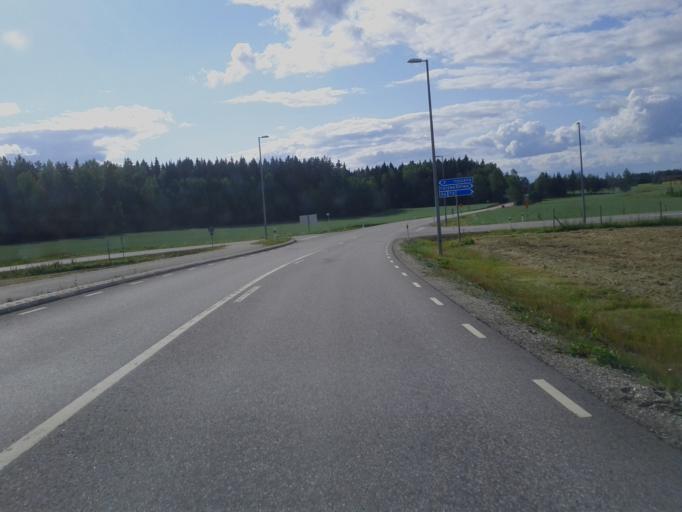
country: SE
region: Vaestmanland
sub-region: Sala Kommun
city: Sala
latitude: 59.9083
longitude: 16.5312
